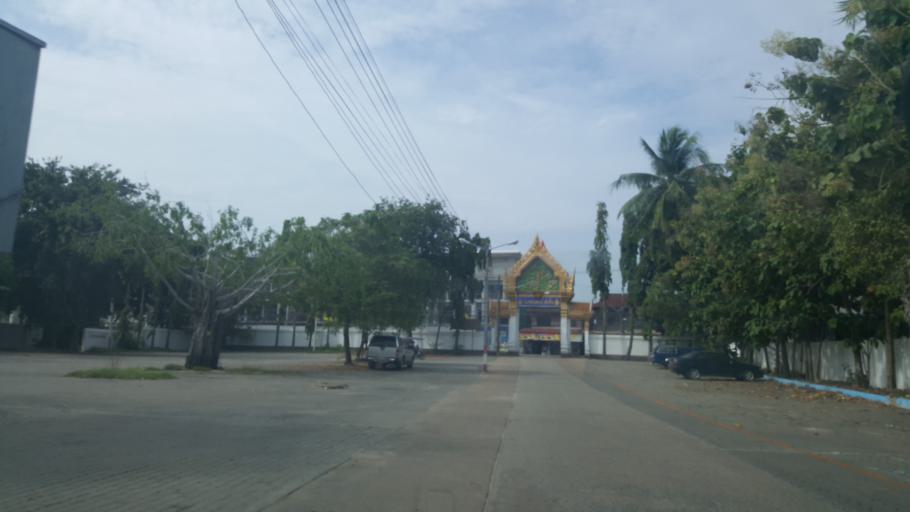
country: TH
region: Chon Buri
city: Sattahip
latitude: 12.6643
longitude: 100.8989
